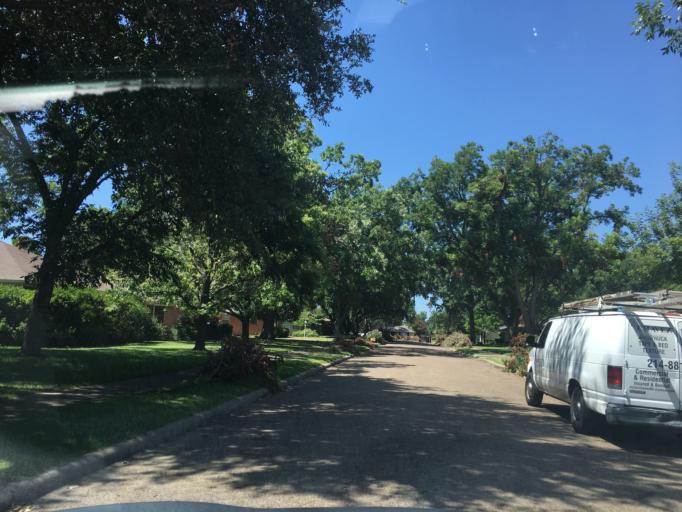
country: US
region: Texas
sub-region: Dallas County
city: Highland Park
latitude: 32.8417
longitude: -96.7440
